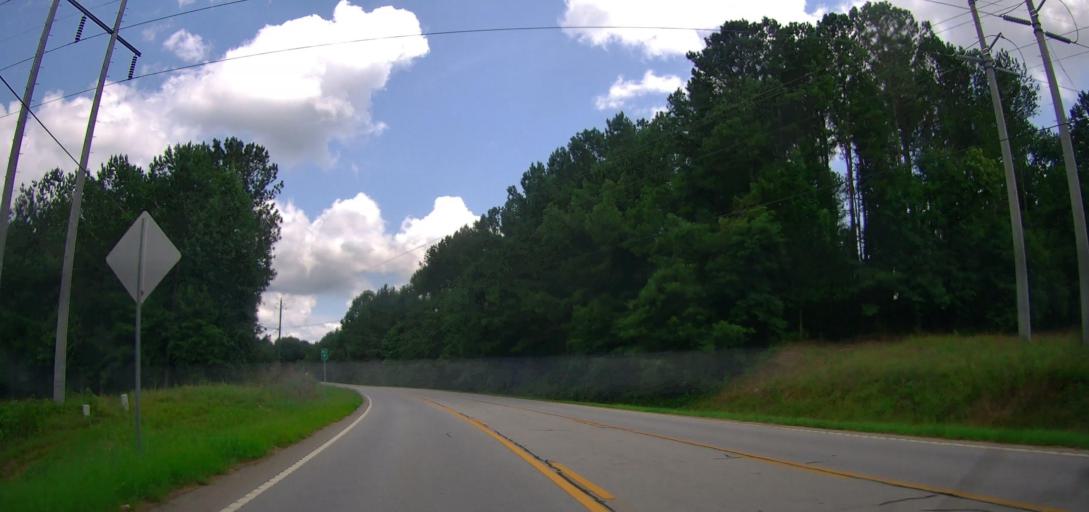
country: US
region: Georgia
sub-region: Heard County
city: Franklin
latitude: 33.2669
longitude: -85.0826
